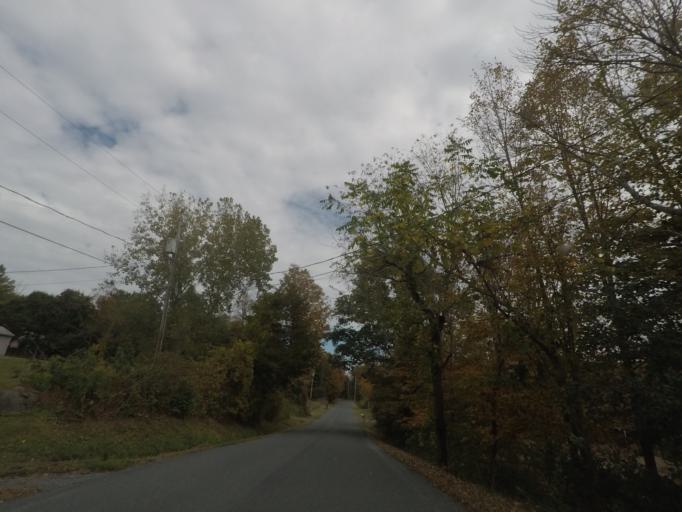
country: US
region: New York
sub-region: Rensselaer County
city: Nassau
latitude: 42.5525
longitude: -73.6469
